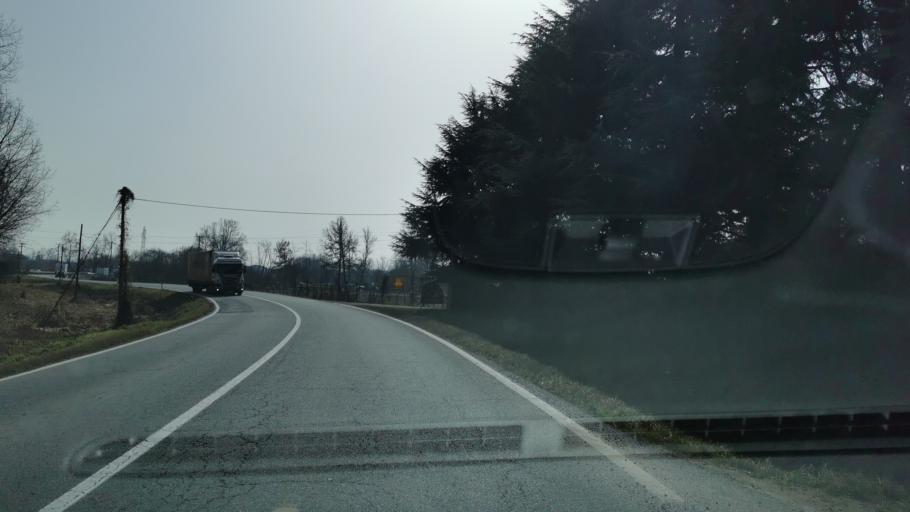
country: IT
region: Piedmont
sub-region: Provincia di Torino
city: San Benigno Canavese
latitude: 45.2157
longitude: 7.7717
